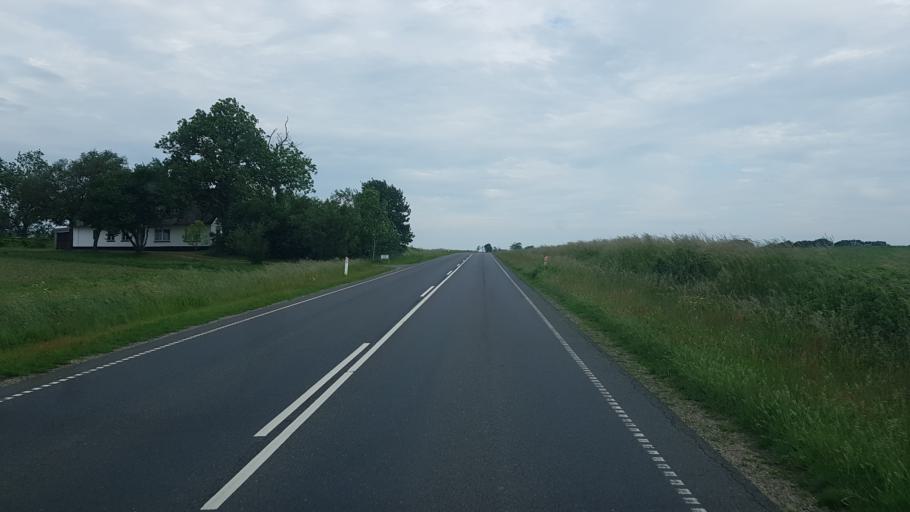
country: DK
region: South Denmark
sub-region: Vejen Kommune
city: Rodding
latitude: 55.3978
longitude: 9.0364
